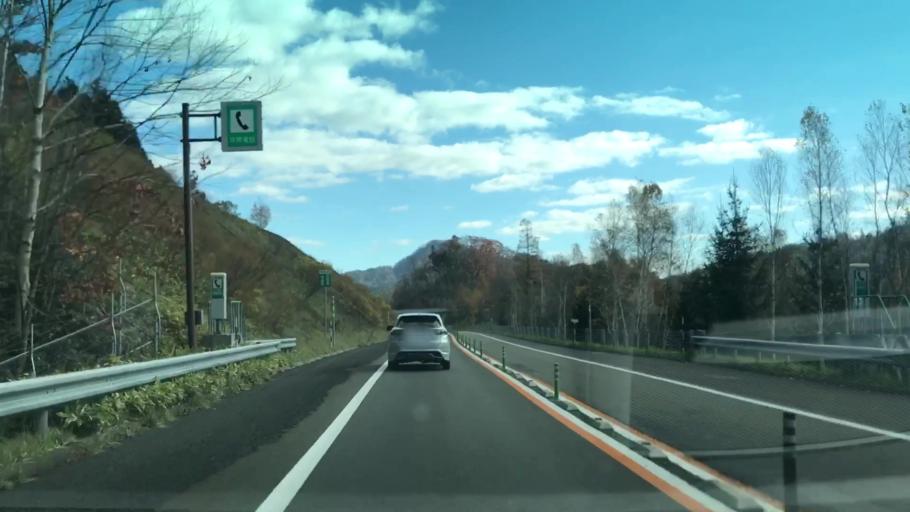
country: JP
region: Hokkaido
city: Chitose
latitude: 42.9111
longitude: 141.9790
